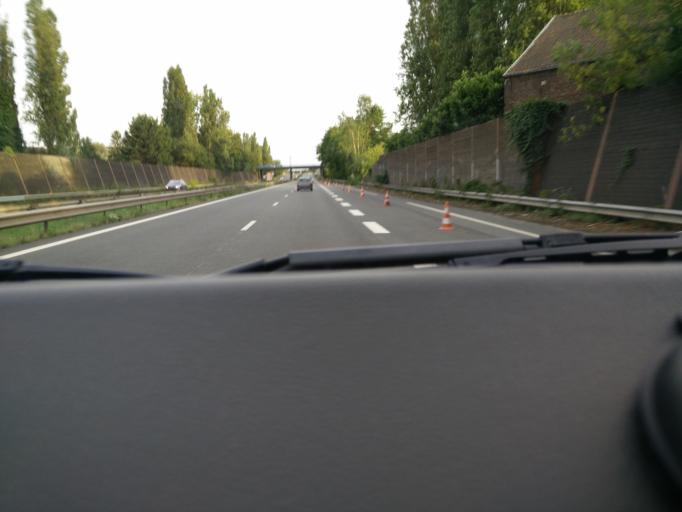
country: FR
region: Nord-Pas-de-Calais
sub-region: Departement du Nord
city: Petite-Foret
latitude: 50.3658
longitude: 3.4839
